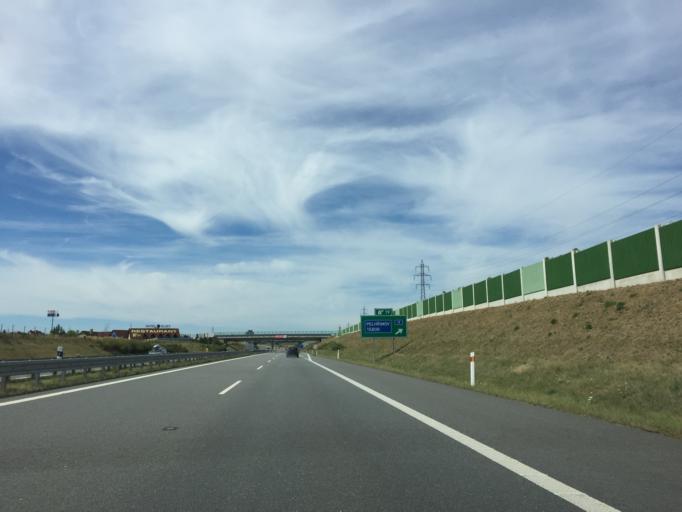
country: CZ
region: Jihocesky
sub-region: Okres Tabor
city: Sezimovo Usti
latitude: 49.4023
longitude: 14.7204
